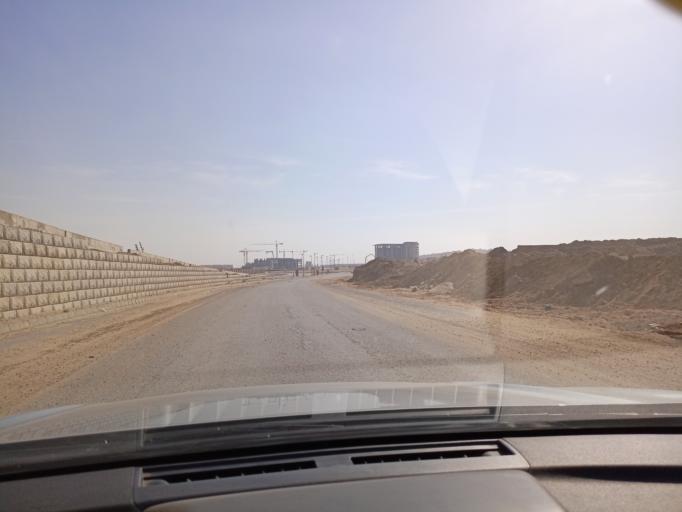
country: EG
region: Muhafazat al Qalyubiyah
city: Al Khankah
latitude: 30.0422
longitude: 31.6860
